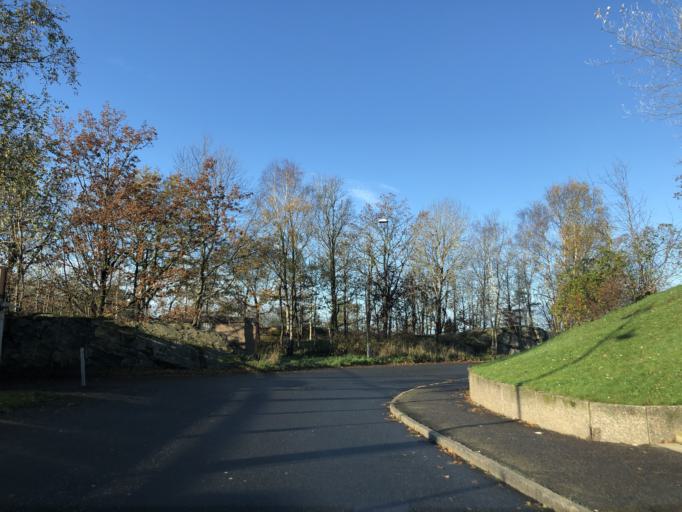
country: SE
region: Vaestra Goetaland
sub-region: Goteborg
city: Gardsten
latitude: 57.7991
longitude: 12.0254
